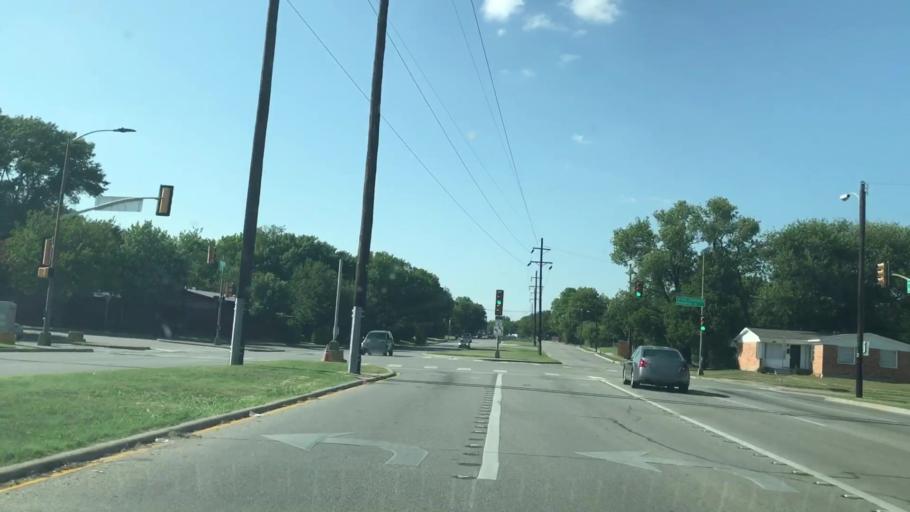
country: US
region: Texas
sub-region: Dallas County
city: Garland
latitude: 32.8347
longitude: -96.6590
